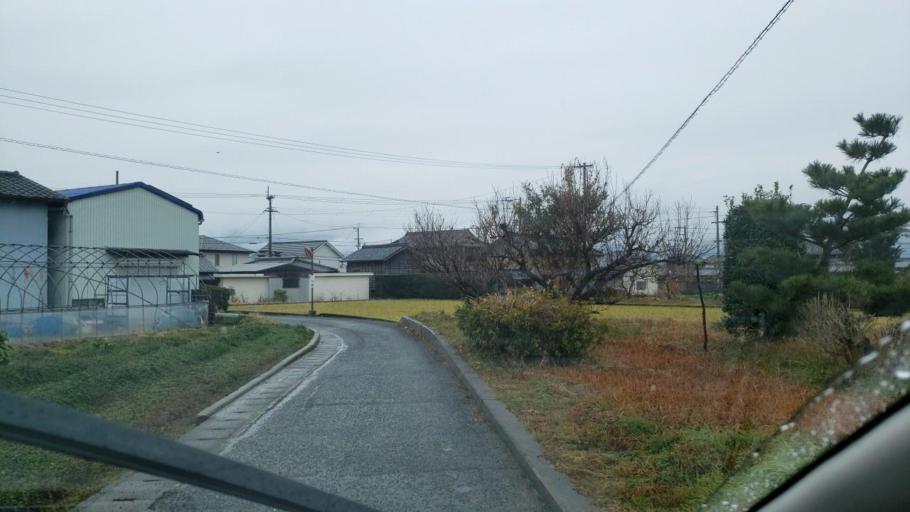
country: JP
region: Tokushima
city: Kamojimacho-jogejima
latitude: 34.0814
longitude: 134.2575
